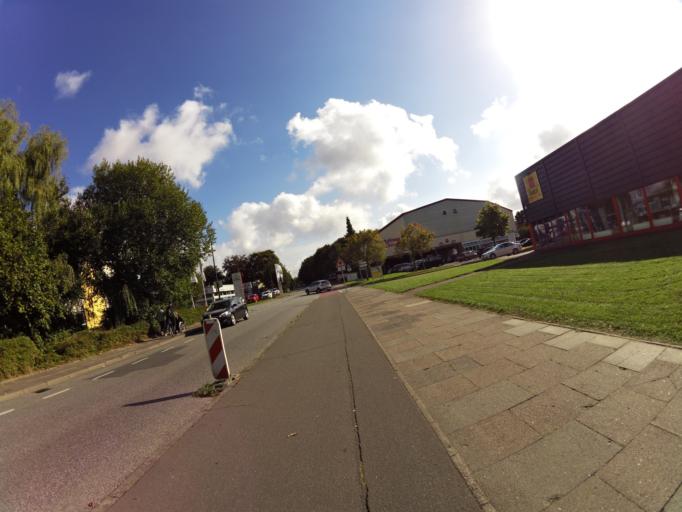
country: DE
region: Schleswig-Holstein
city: Eckernforde
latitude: 54.4497
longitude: 9.8359
